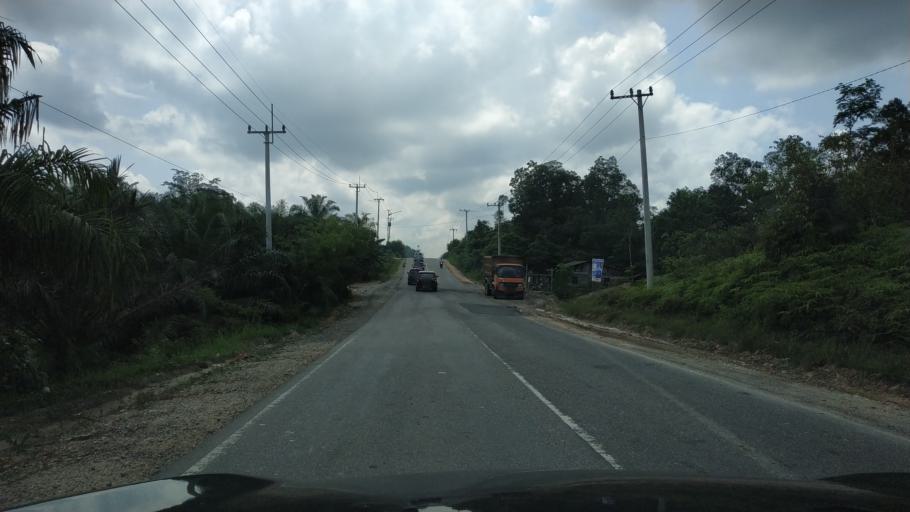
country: ID
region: Riau
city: Pangkalanbunut
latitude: 0.3021
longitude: 101.9151
